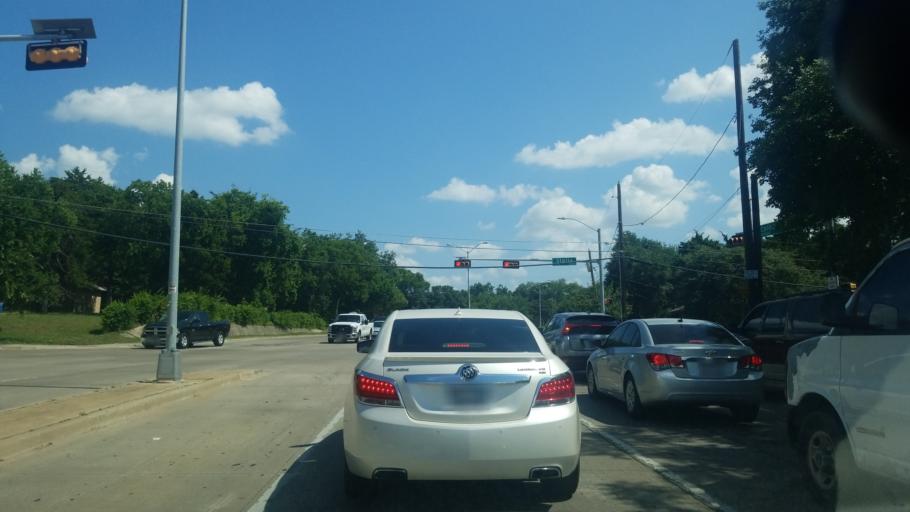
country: US
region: Texas
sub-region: Dallas County
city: Dallas
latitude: 32.7291
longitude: -96.7991
